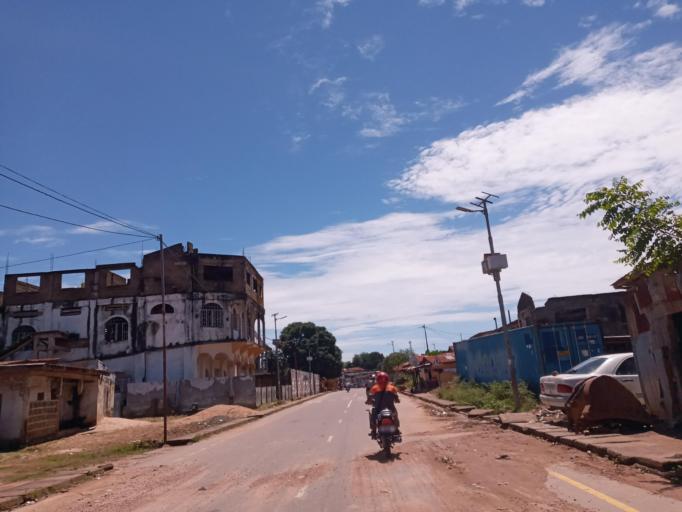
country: SL
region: Eastern Province
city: Koidu
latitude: 8.6406
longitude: -10.9748
